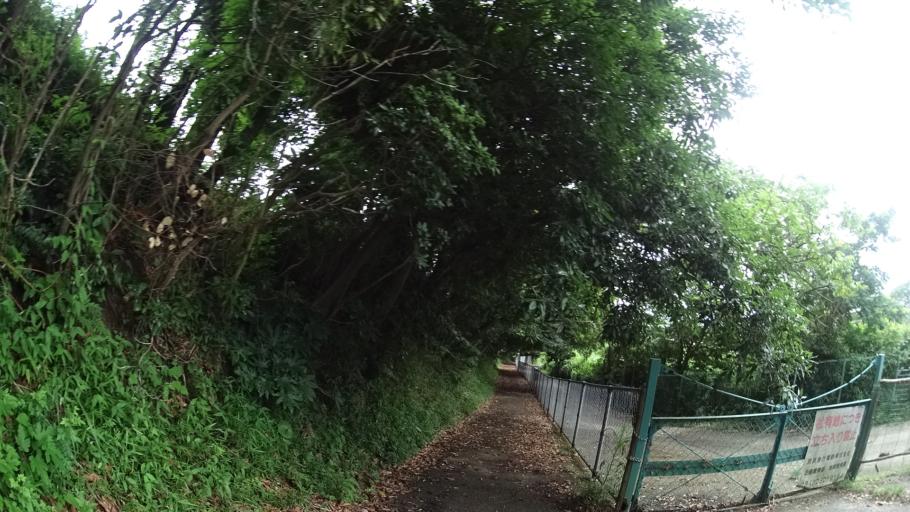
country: JP
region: Kanagawa
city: Yokosuka
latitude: 35.2129
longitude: 139.6565
